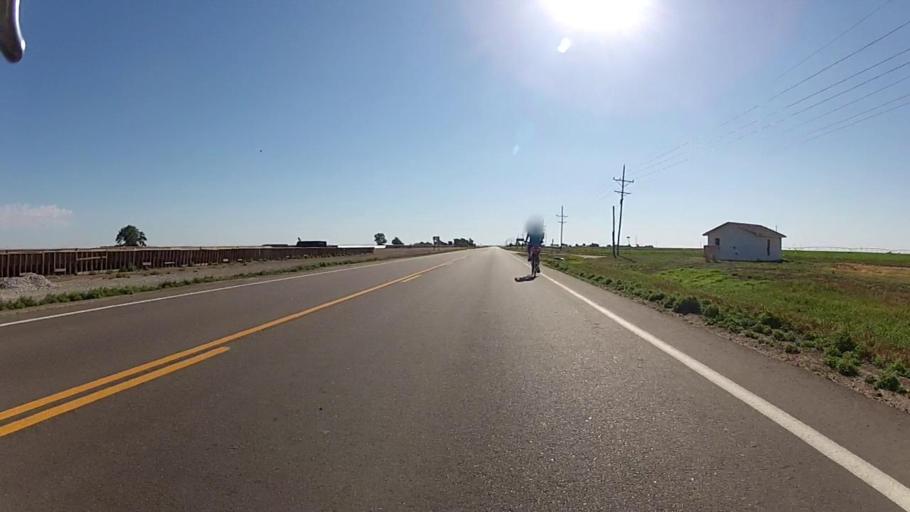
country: US
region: Kansas
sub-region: Haskell County
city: Sublette
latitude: 37.5441
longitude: -100.6248
